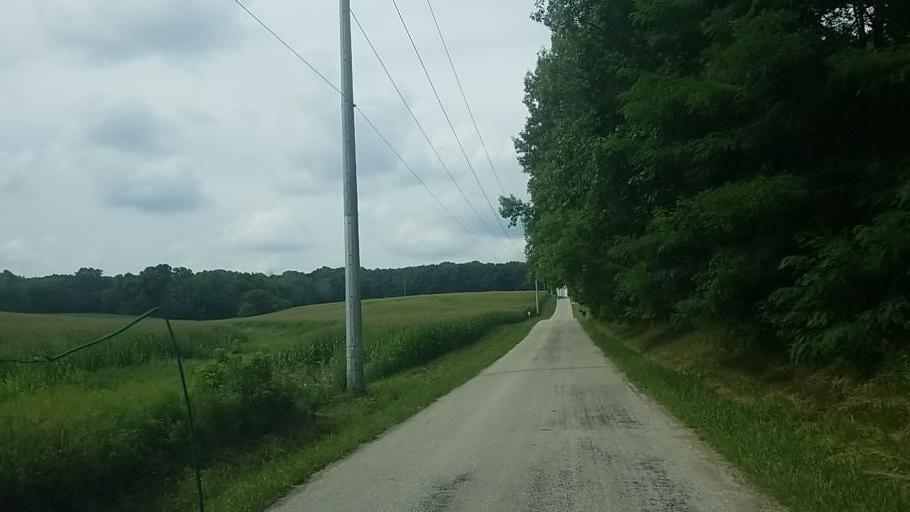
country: US
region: Ohio
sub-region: Knox County
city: Fredericktown
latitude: 40.5522
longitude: -82.5474
